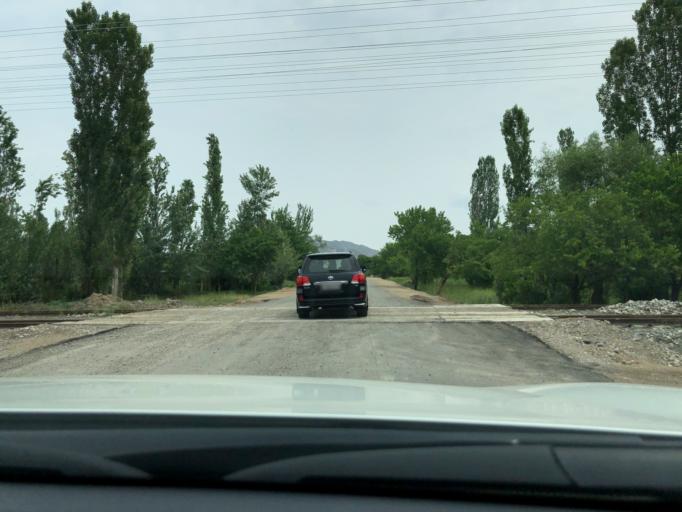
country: TJ
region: Viloyati Sughd
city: Isfara
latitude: 40.1501
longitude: 70.6167
